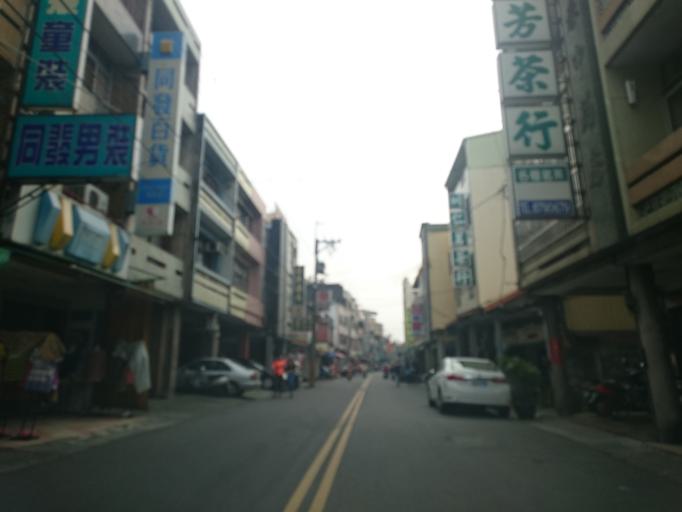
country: TW
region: Taiwan
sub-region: Nantou
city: Nantou
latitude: 23.8122
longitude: 120.6171
